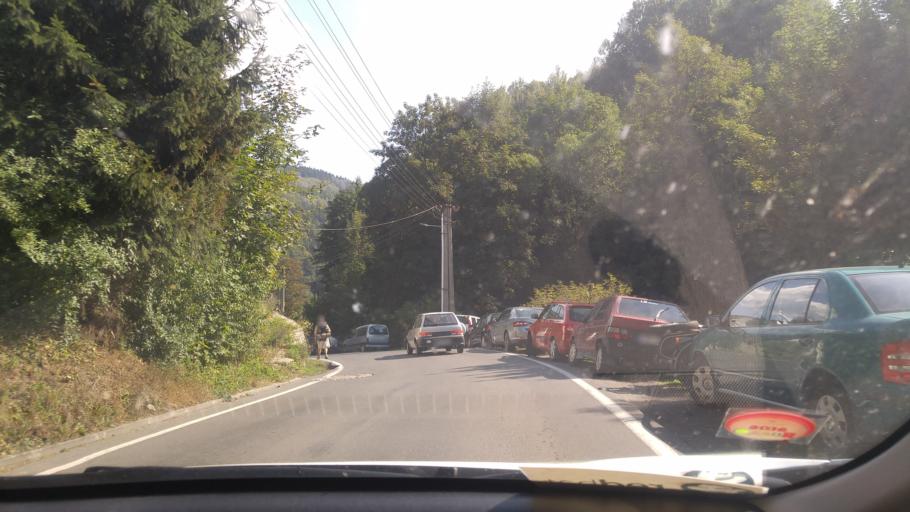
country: CZ
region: Olomoucky
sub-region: Okres Sumperk
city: Stare Mesto
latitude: 50.1505
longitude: 17.0087
